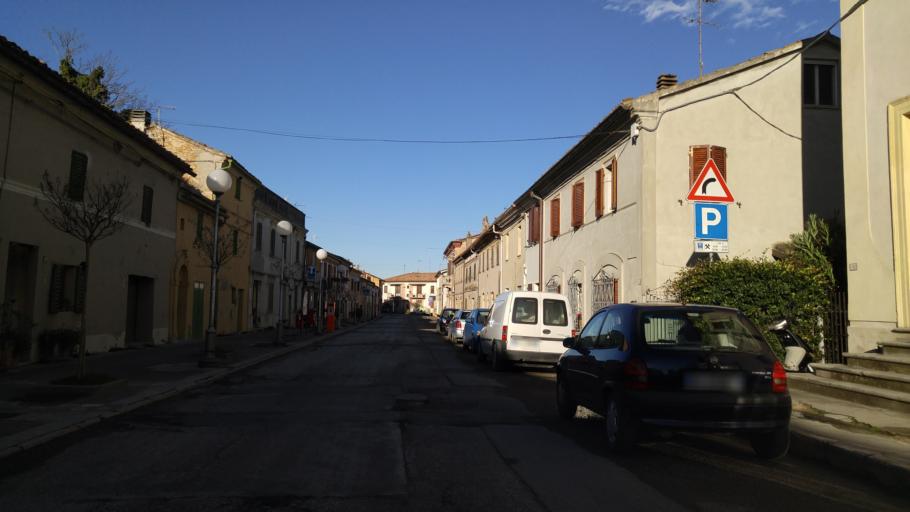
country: IT
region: The Marches
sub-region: Provincia di Pesaro e Urbino
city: Bellocchi
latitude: 43.7529
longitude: 13.0134
